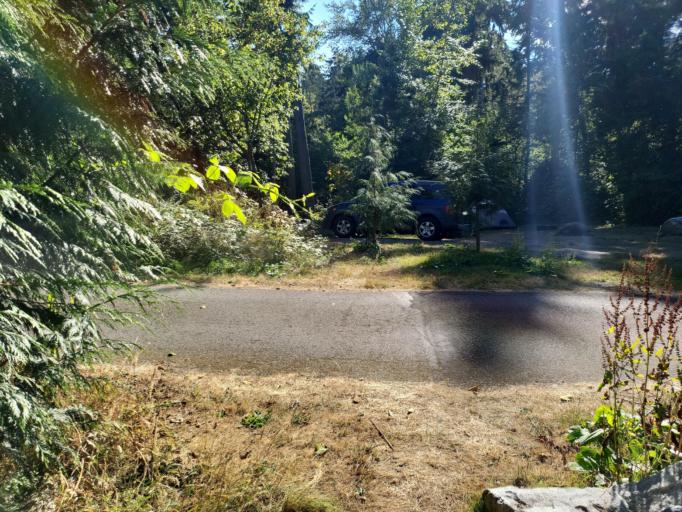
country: US
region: Washington
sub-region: Pierce County
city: Tacoma
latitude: 47.3155
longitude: -122.4062
